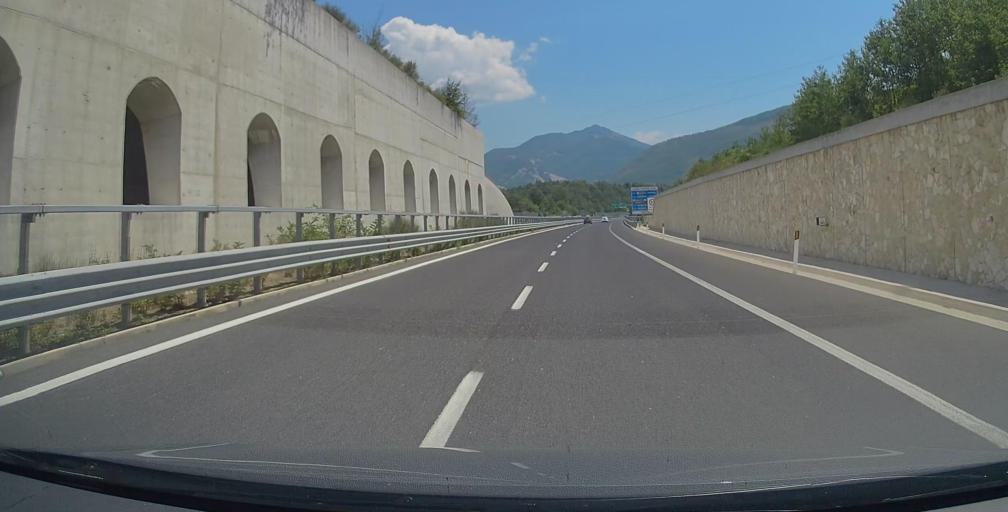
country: IT
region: Basilicate
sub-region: Provincia di Potenza
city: Lauria
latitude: 40.0846
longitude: 15.8487
